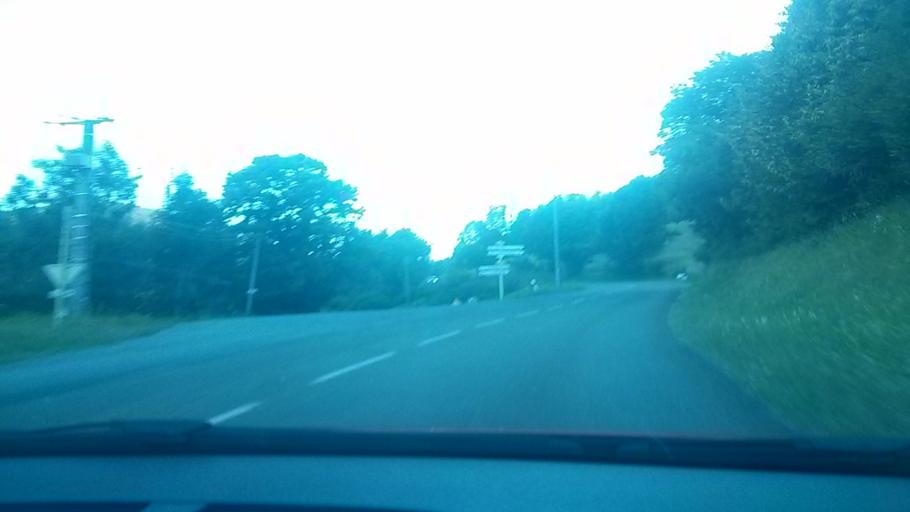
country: FR
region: Franche-Comte
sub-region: Departement du Jura
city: Saint-Claude
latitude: 46.3515
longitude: 5.8396
